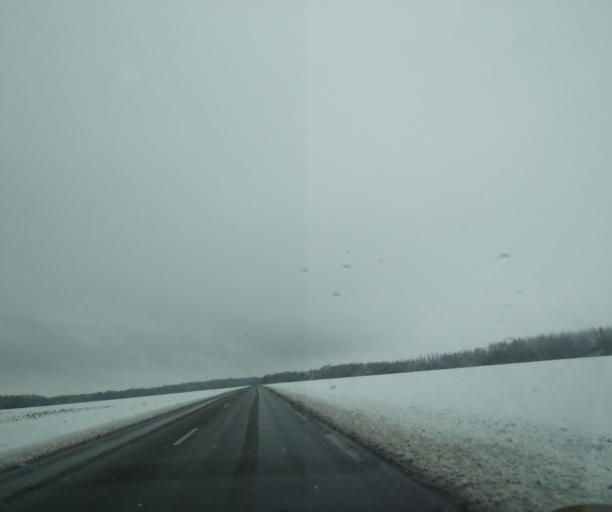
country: FR
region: Champagne-Ardenne
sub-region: Departement de la Haute-Marne
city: Montier-en-Der
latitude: 48.5001
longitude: 4.7862
